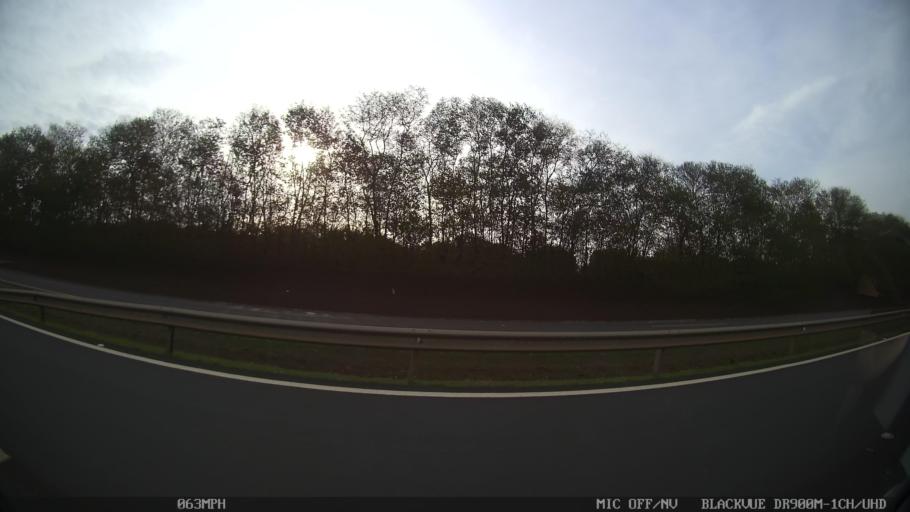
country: BR
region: Sao Paulo
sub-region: Iracemapolis
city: Iracemapolis
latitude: -22.6654
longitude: -47.5348
